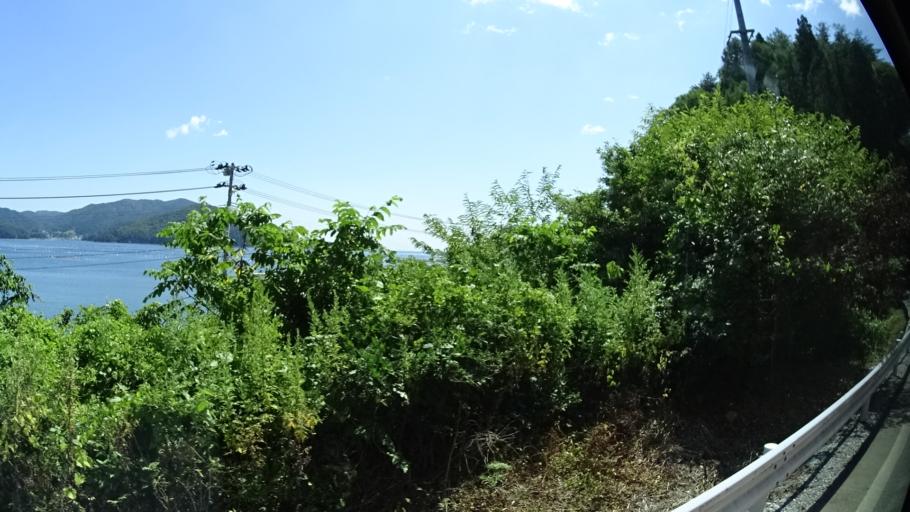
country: JP
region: Iwate
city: Ofunato
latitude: 39.0239
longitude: 141.7092
